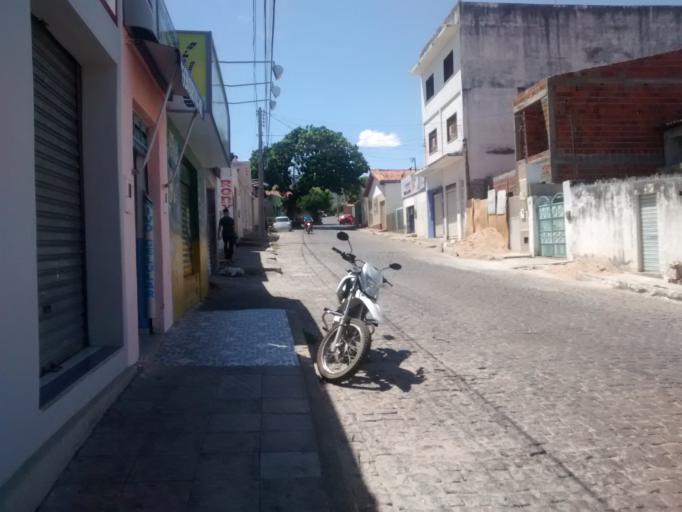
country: BR
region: Bahia
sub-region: Brumado
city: Brumado
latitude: -14.2096
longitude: -41.6701
